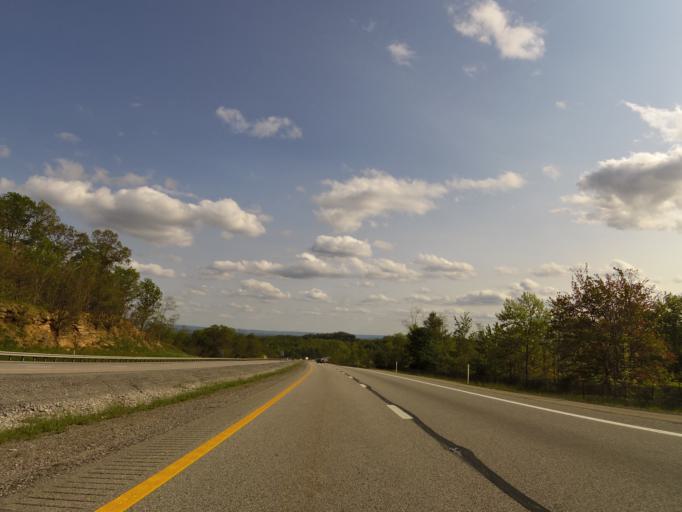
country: US
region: West Virginia
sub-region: Raleigh County
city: Shady Spring
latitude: 37.5615
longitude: -81.1135
